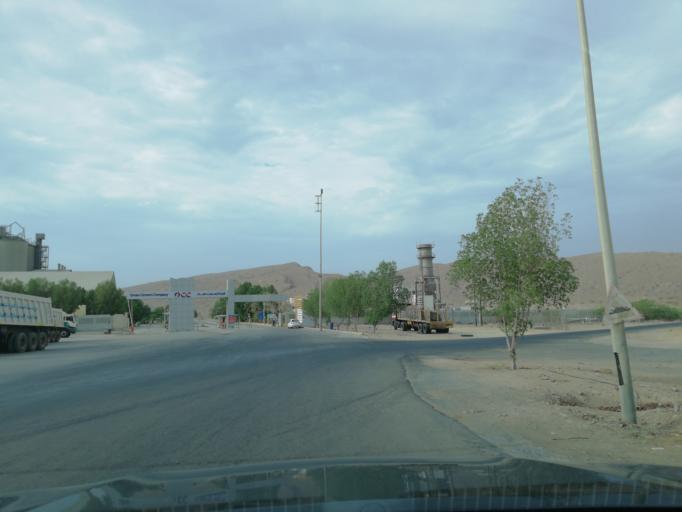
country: OM
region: Muhafazat Masqat
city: Bawshar
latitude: 23.4814
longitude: 58.2871
